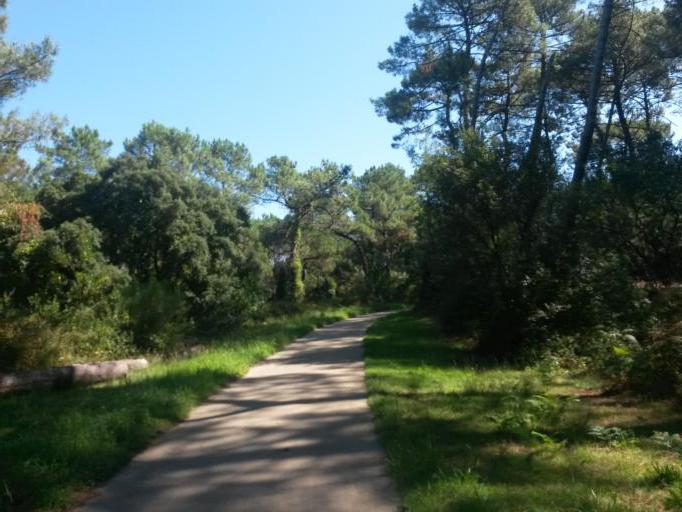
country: FR
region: Aquitaine
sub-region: Departement des Pyrenees-Atlantiques
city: Boucau
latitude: 43.5158
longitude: -1.4964
